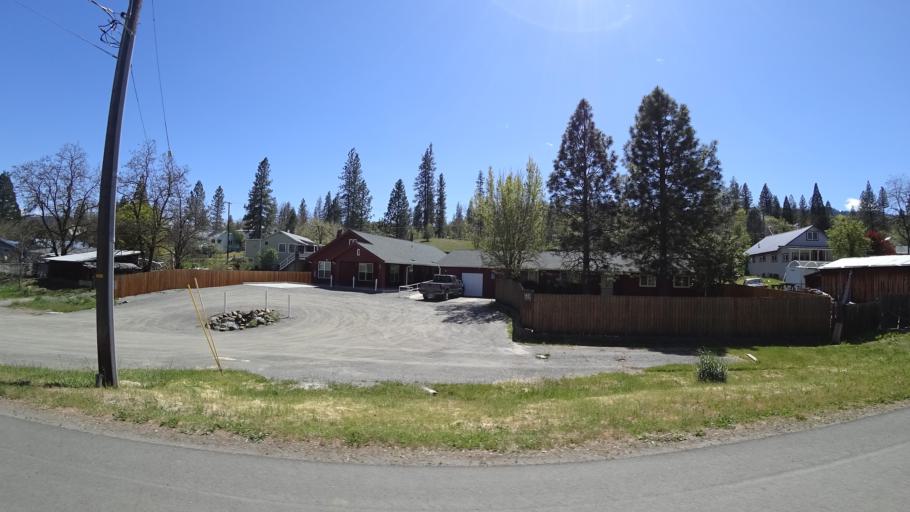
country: US
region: California
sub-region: Trinity County
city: Weaverville
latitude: 40.7359
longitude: -122.9464
